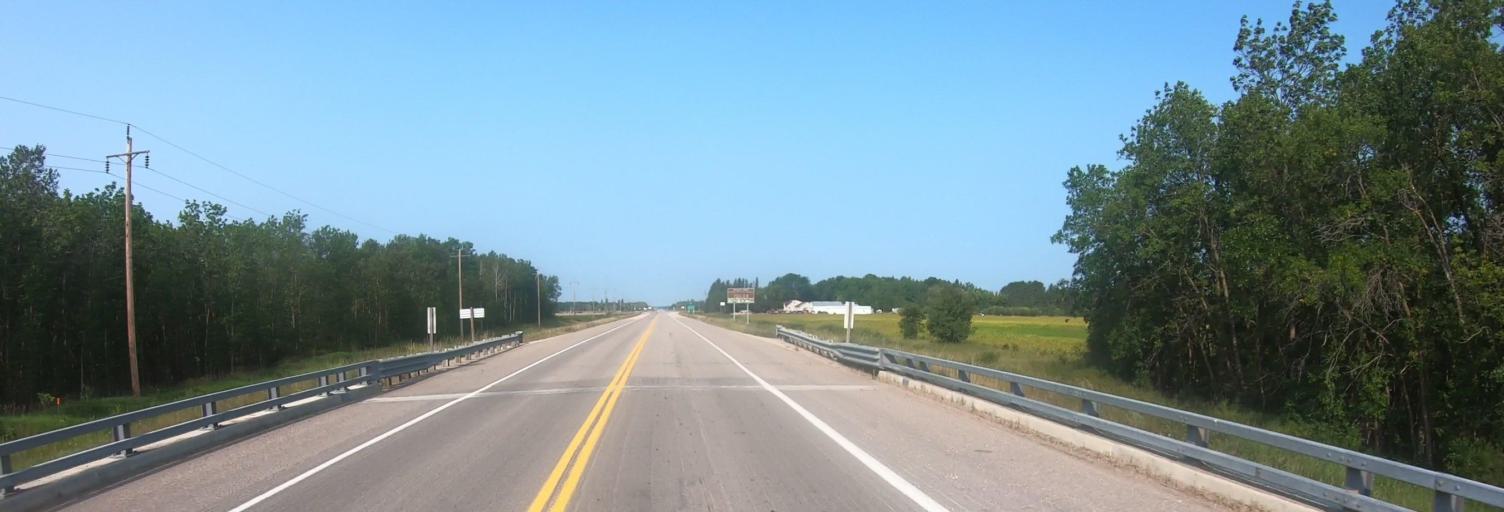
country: US
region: Minnesota
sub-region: Roseau County
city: Roseau
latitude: 49.0234
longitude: -95.6363
